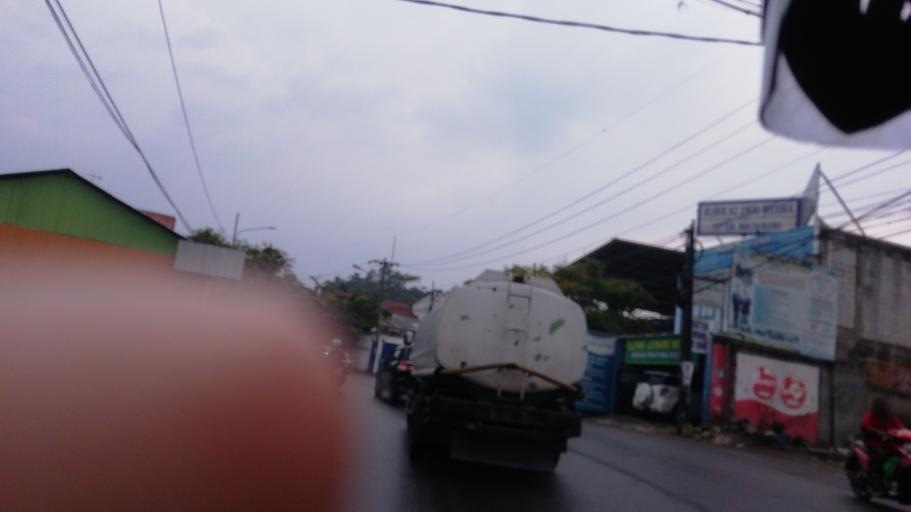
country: ID
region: West Java
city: Bogor
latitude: -6.5382
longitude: 106.8063
